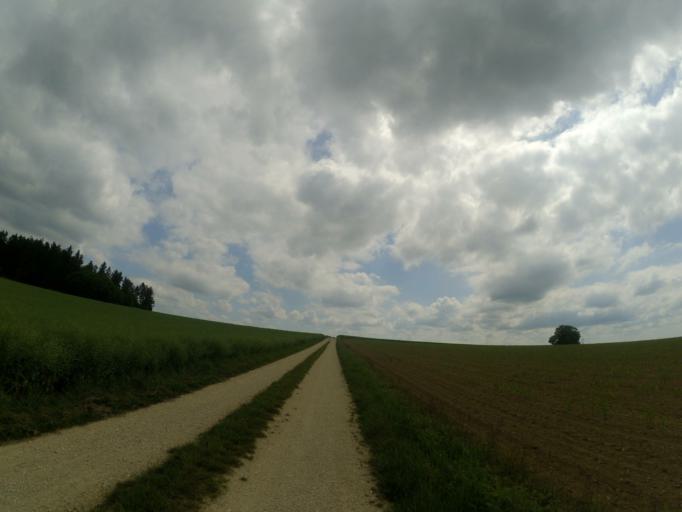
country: DE
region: Baden-Wuerttemberg
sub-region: Tuebingen Region
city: Blaubeuren
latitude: 48.4231
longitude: 9.8296
